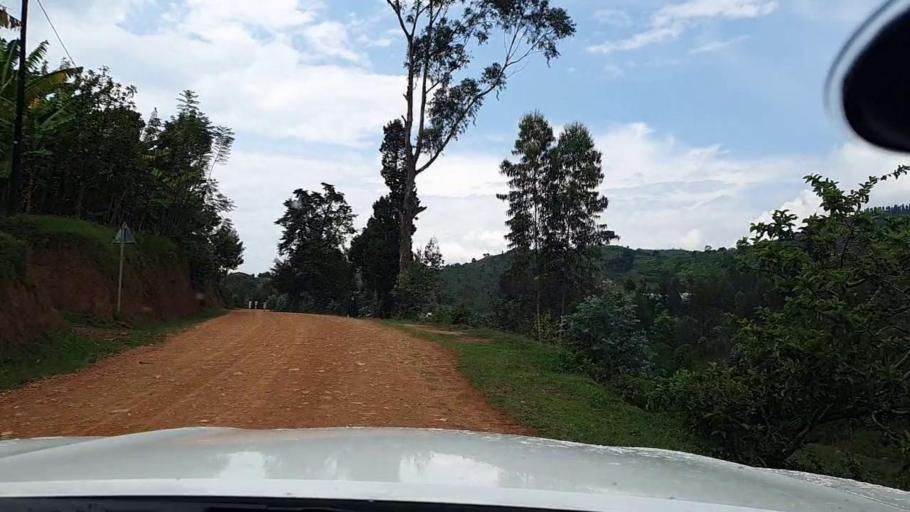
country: RW
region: Western Province
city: Kibuye
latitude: -2.1110
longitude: 29.4203
